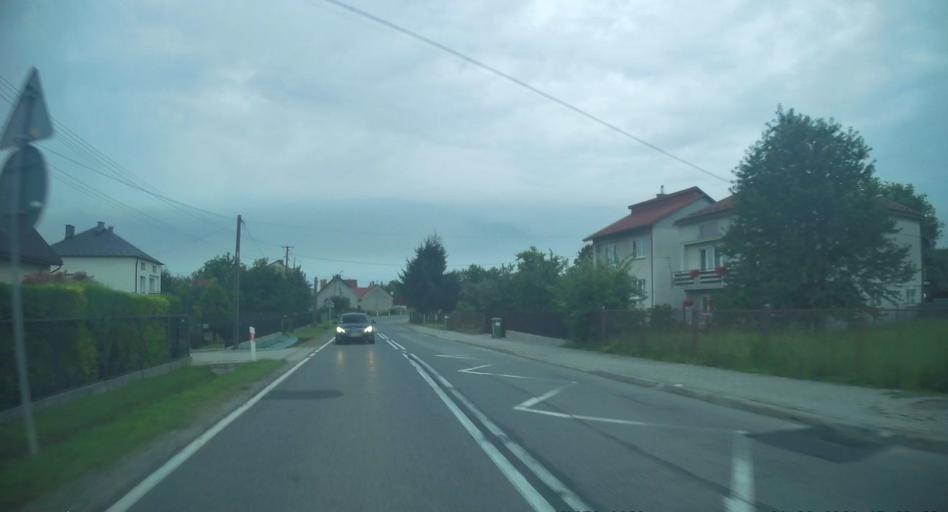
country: PL
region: Lesser Poland Voivodeship
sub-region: Powiat tarnowski
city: Wierzchoslawice
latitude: 49.9974
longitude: 20.8536
